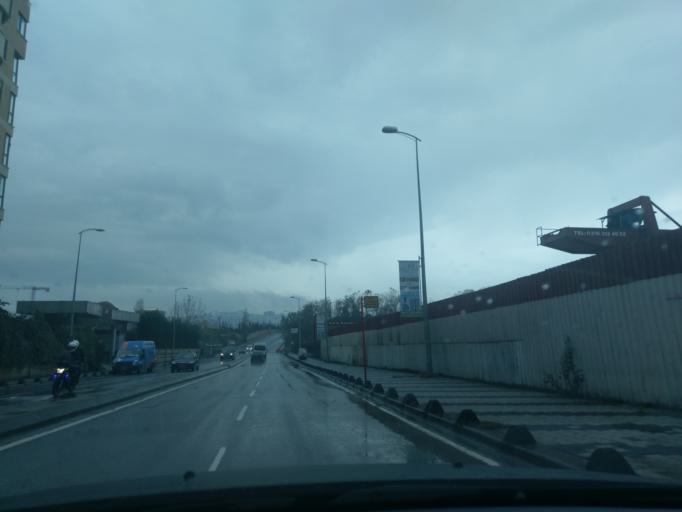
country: TR
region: Istanbul
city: Sancaktepe
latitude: 41.0254
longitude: 29.2369
